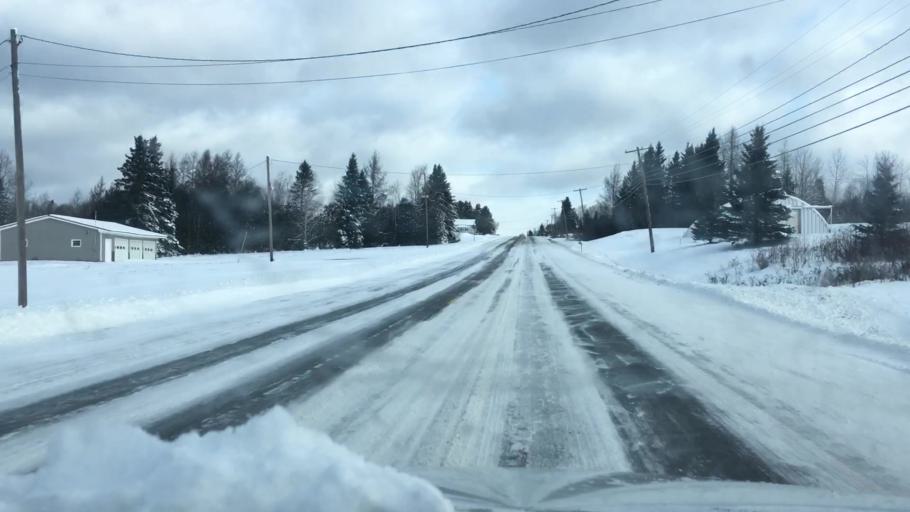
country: US
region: Maine
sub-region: Aroostook County
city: Caribou
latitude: 46.9816
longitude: -68.0335
